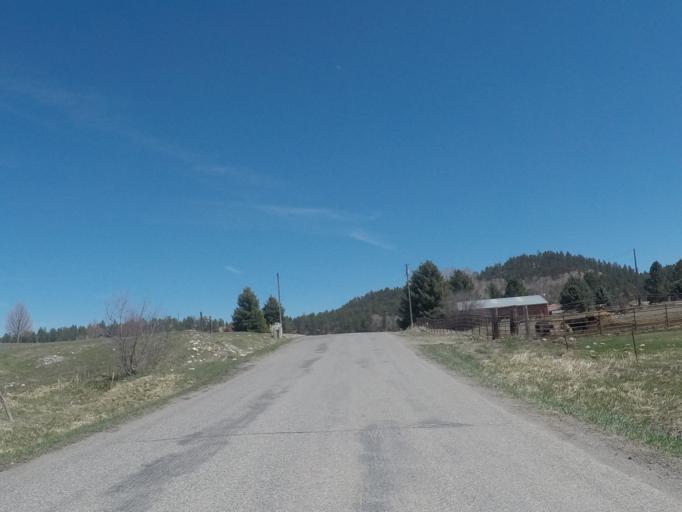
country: US
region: Montana
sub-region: Stillwater County
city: Columbus
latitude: 45.6240
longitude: -109.2823
